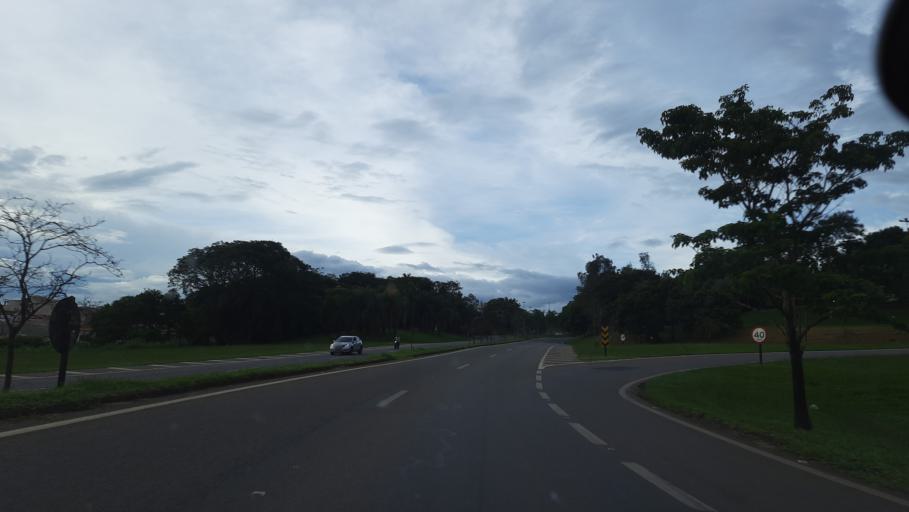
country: BR
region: Sao Paulo
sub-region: Sao Joao Da Boa Vista
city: Sao Joao da Boa Vista
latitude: -21.9912
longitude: -46.7931
